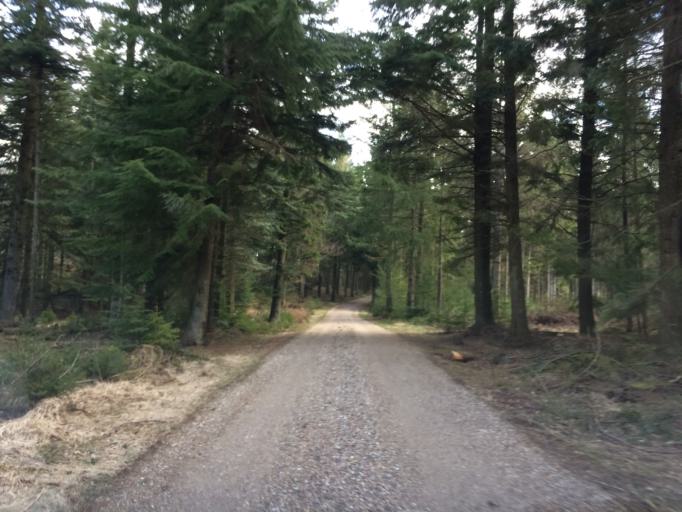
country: DK
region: Central Jutland
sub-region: Holstebro Kommune
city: Ulfborg
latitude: 56.2626
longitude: 8.4425
